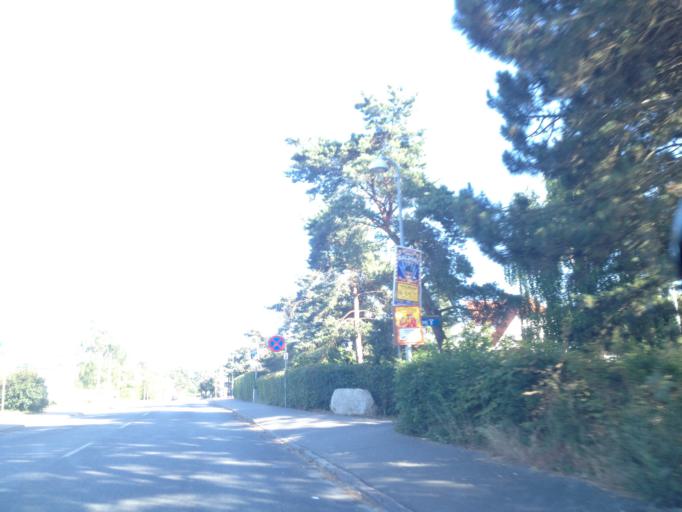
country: DK
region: Capital Region
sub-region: Halsnaes Kommune
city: Frederiksvaerk
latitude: 56.0595
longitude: 12.0755
